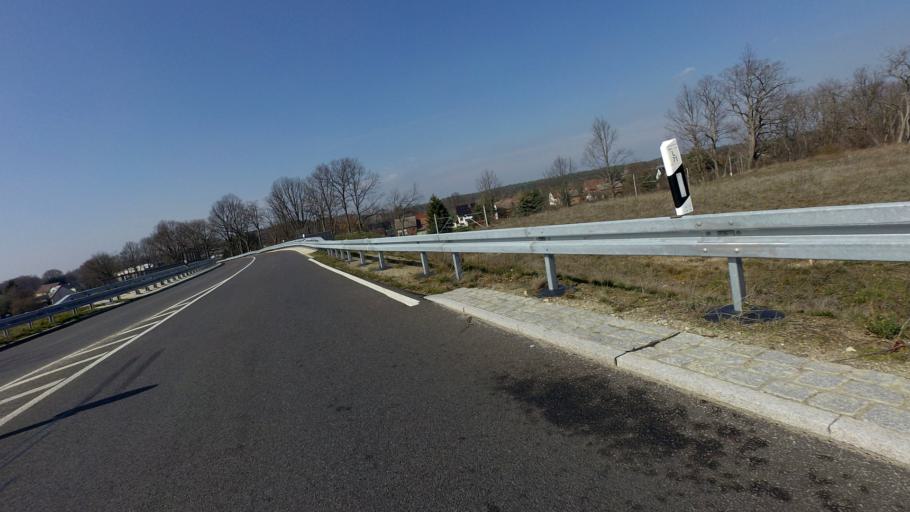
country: DE
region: Brandenburg
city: Drahnsdorf
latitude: 51.9171
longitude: 13.5827
